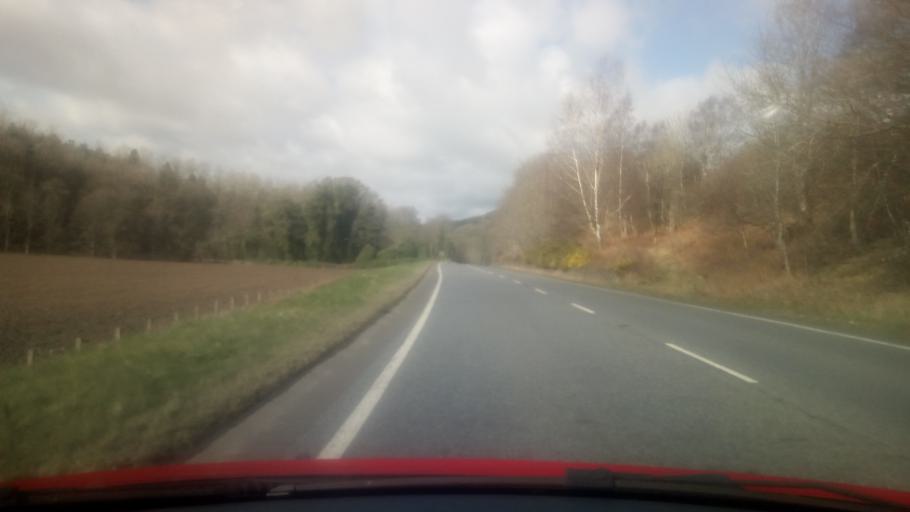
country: GB
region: Scotland
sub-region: The Scottish Borders
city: Selkirk
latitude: 55.6154
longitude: -2.9181
